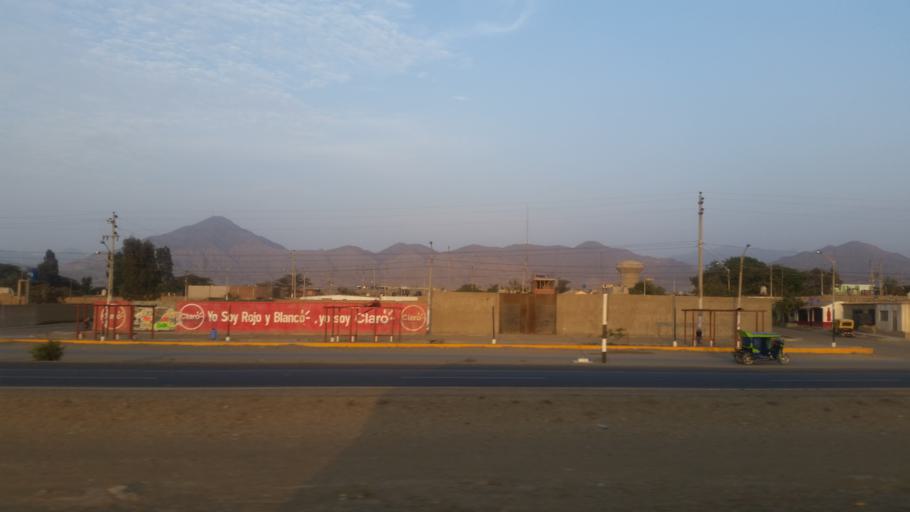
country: PE
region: La Libertad
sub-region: Ascope
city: Chicama
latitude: -7.8635
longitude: -79.1387
